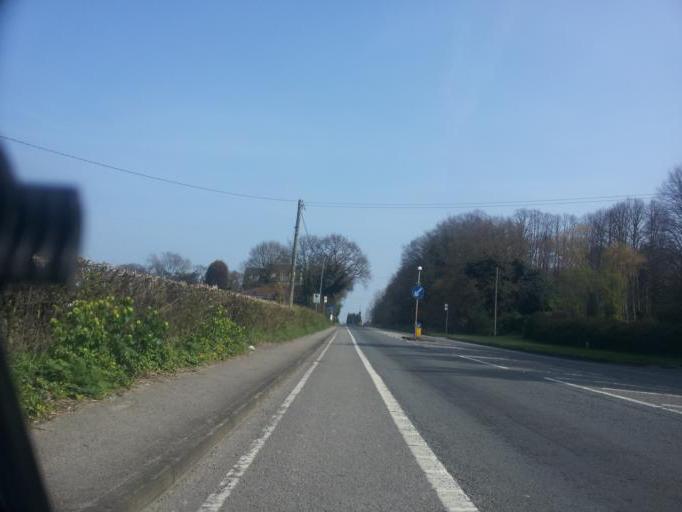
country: GB
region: England
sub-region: Medway
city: Cuxton
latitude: 51.4169
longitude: 0.4458
